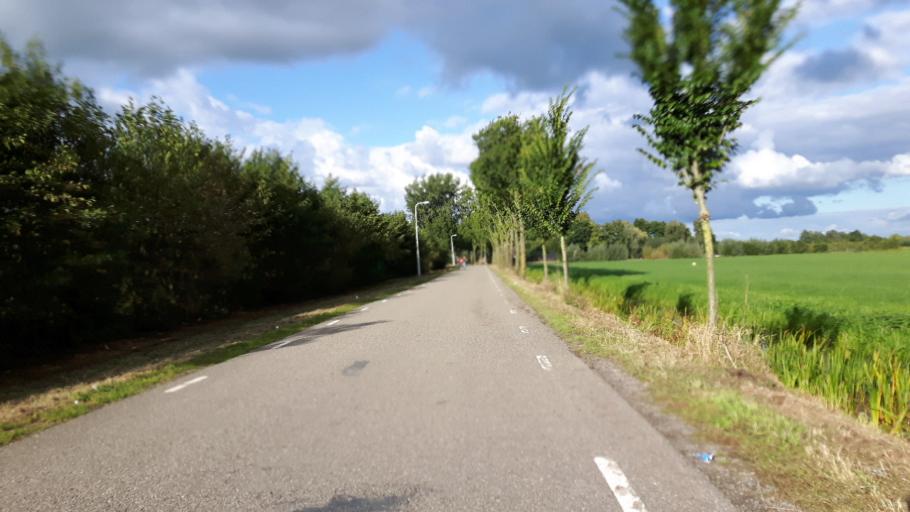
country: NL
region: Utrecht
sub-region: Gemeente Vianen
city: Vianen
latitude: 51.9505
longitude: 5.0741
